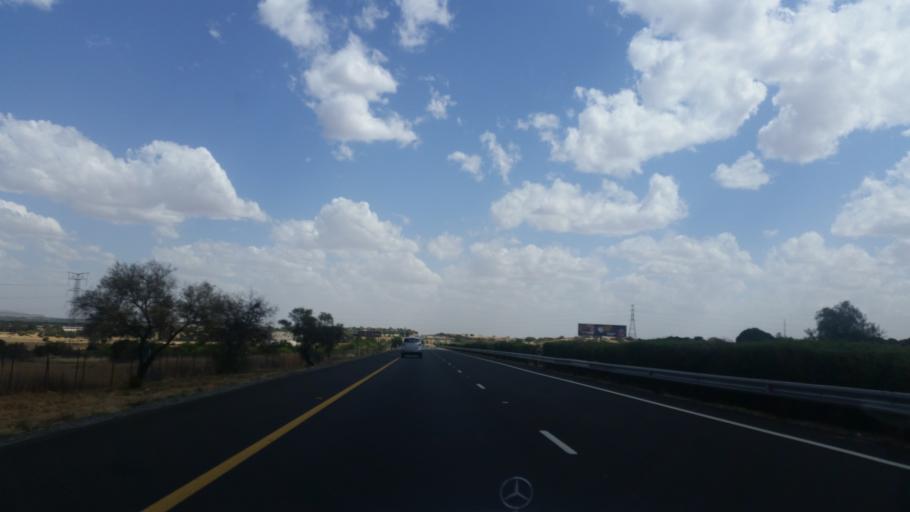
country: ZA
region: Orange Free State
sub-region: Mangaung Metropolitan Municipality
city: Bloemfontein
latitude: -29.0818
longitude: 26.1773
